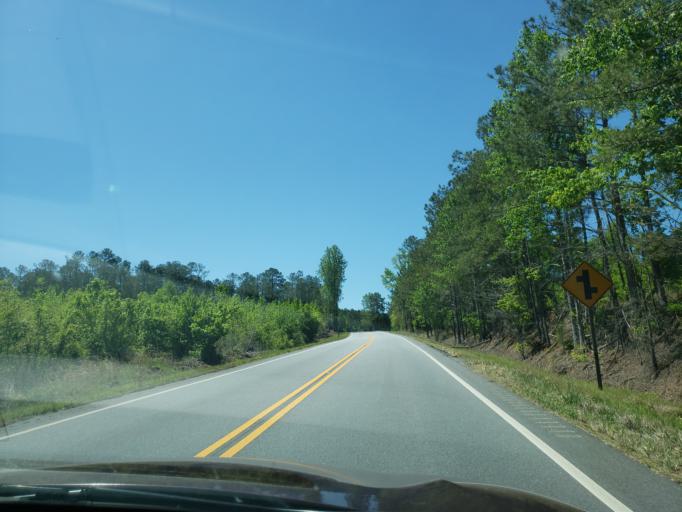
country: US
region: Alabama
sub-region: Tallapoosa County
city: Dadeville
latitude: 32.6765
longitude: -85.7896
